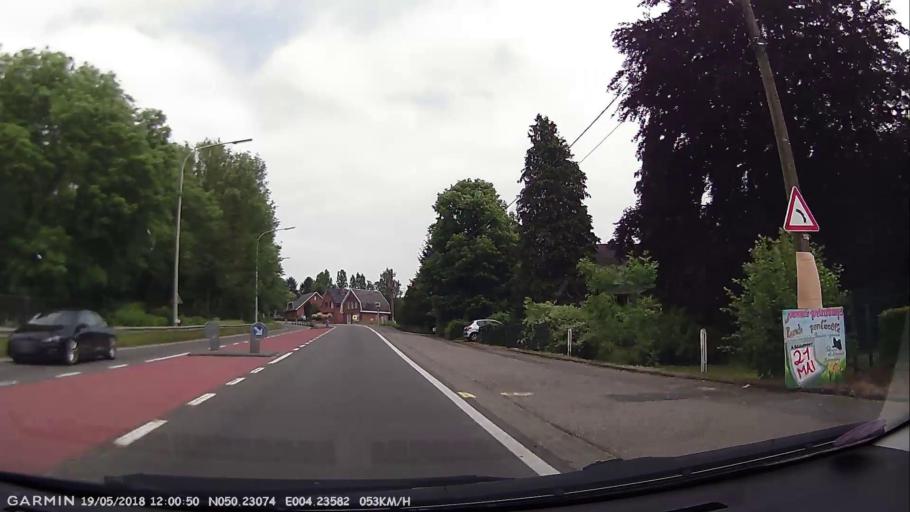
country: BE
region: Wallonia
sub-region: Province du Hainaut
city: Beaumont
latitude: 50.2308
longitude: 4.2359
